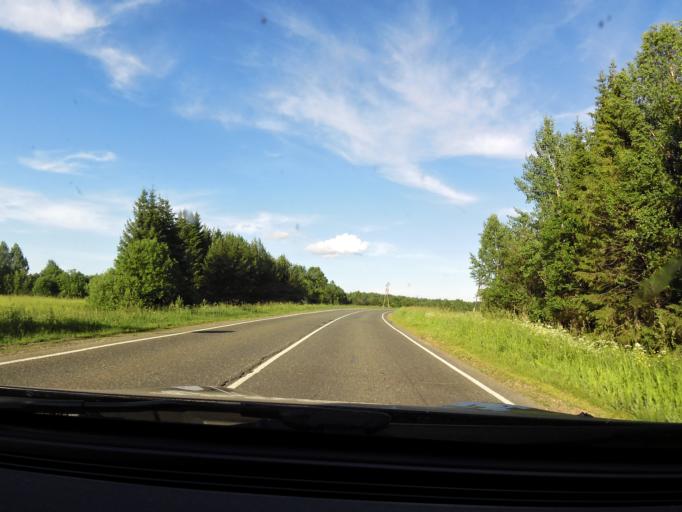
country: RU
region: Kirov
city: Belorechensk
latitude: 58.8081
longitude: 52.4608
